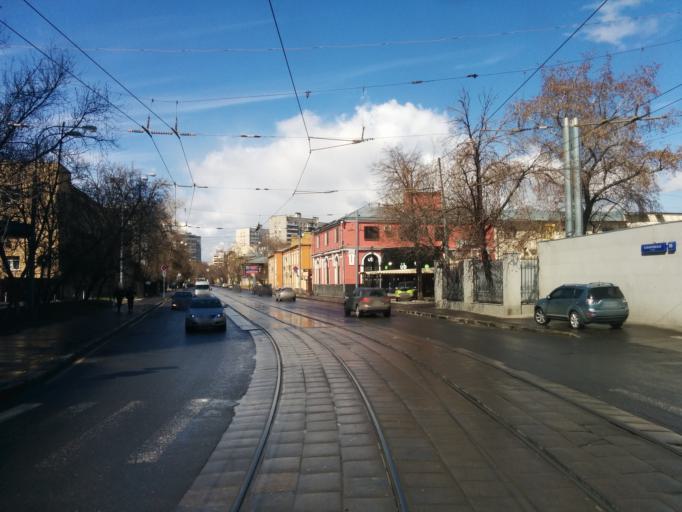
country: RU
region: Moscow
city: Sokol'niki
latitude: 55.7773
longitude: 37.6484
